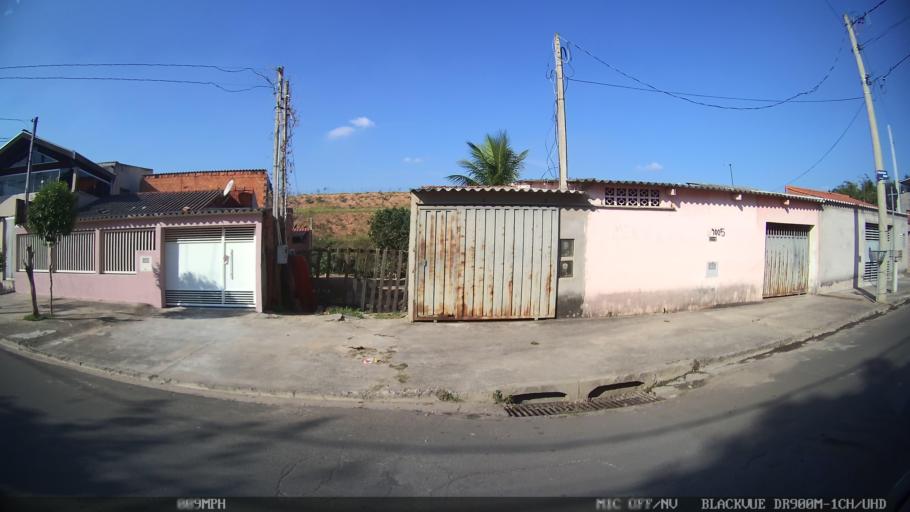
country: BR
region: Sao Paulo
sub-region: Indaiatuba
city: Indaiatuba
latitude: -22.9976
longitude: -47.1366
